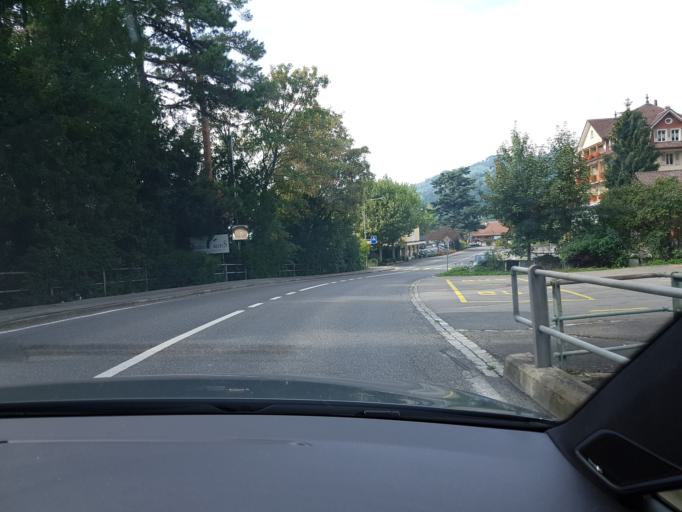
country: CH
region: Bern
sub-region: Thun District
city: Sigriswil
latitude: 46.6955
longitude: 7.7388
